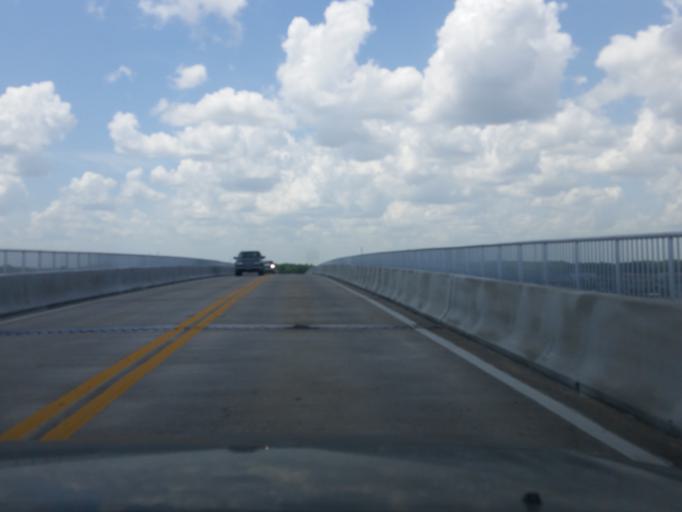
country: US
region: Florida
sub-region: Santa Rosa County
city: Navarre
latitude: 30.3965
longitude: -86.8632
